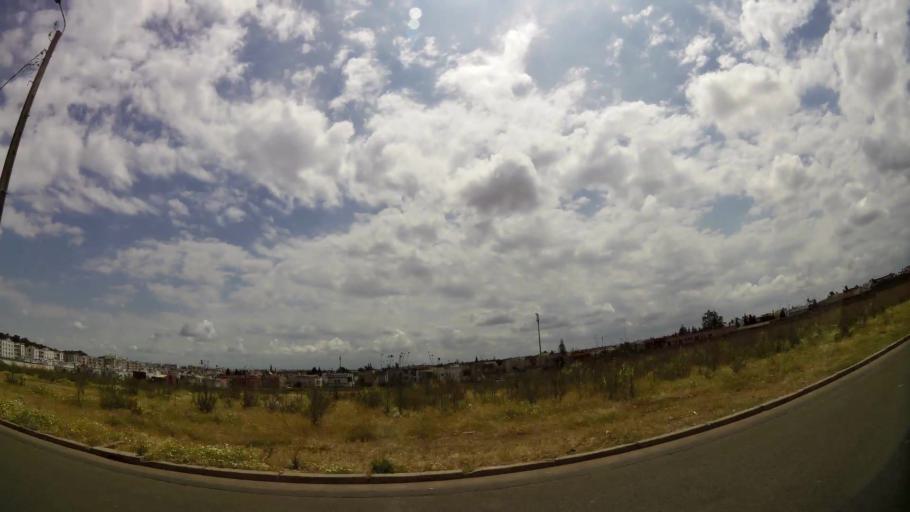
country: MA
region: Gharb-Chrarda-Beni Hssen
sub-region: Kenitra Province
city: Kenitra
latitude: 34.2450
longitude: -6.6098
